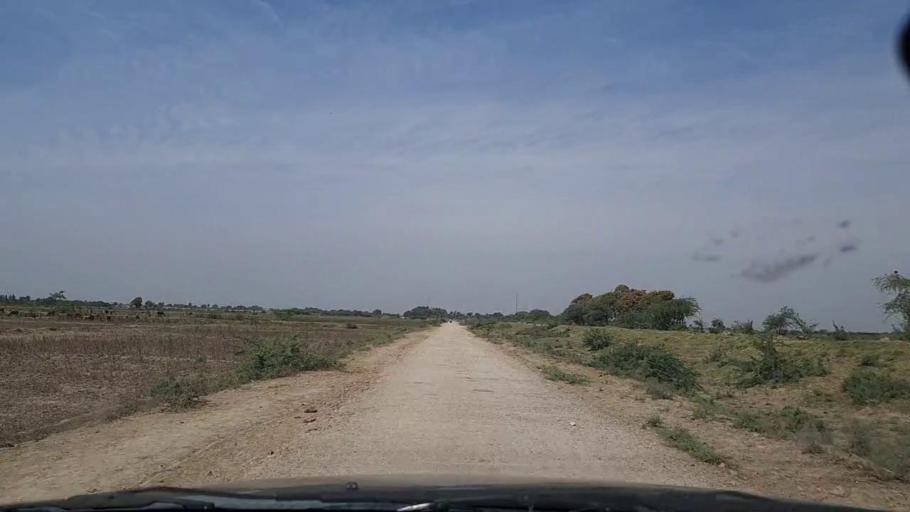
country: PK
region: Sindh
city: Mirpur Batoro
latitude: 24.6491
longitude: 68.1854
